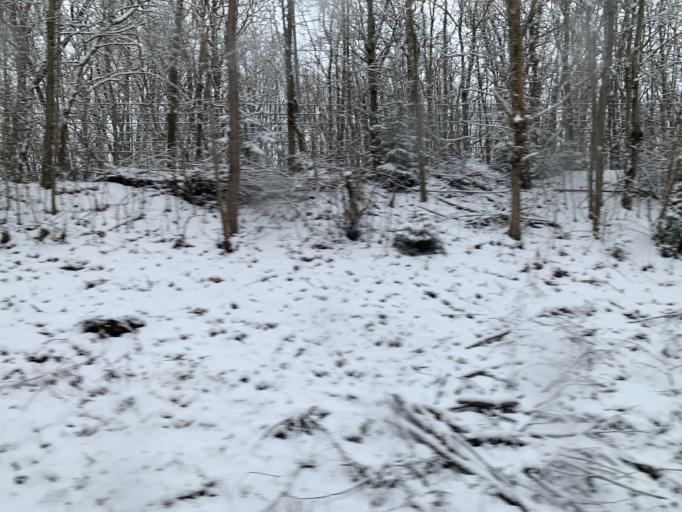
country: DE
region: Bavaria
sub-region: Upper Bavaria
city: Unterhaching
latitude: 48.0892
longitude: 11.6073
